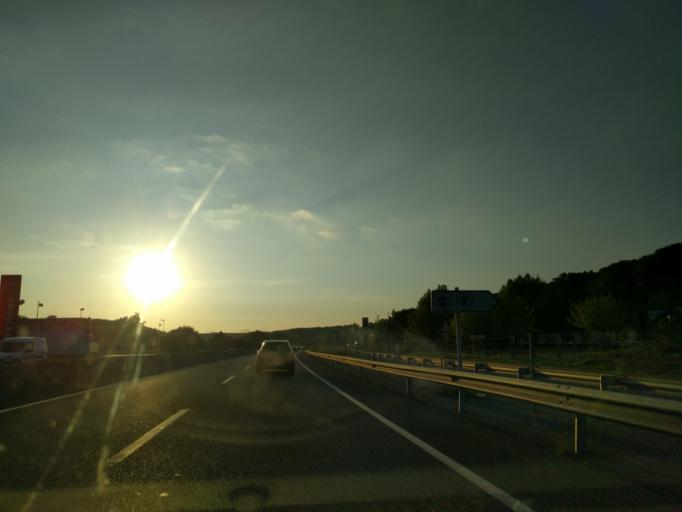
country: ES
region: Catalonia
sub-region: Provincia de Girona
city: Santa Cristina d'Aro
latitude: 41.8270
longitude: 2.9490
